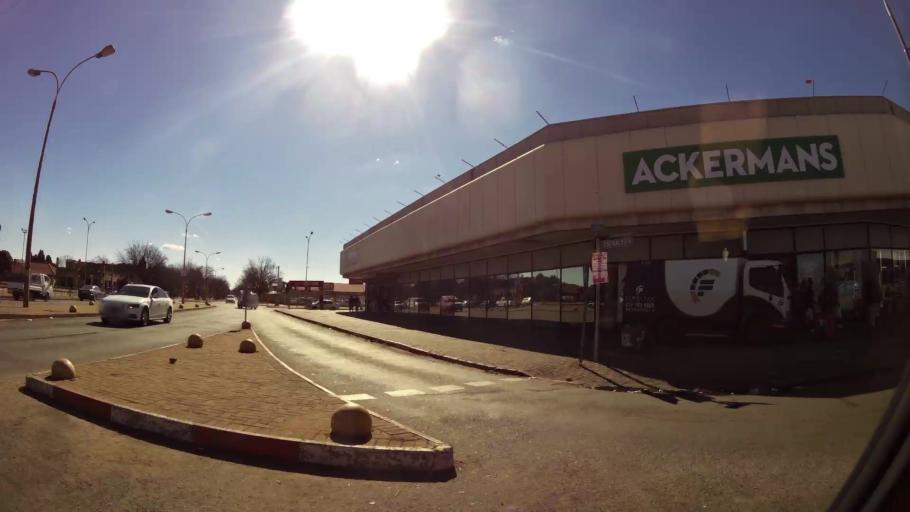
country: ZA
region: Gauteng
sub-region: West Rand District Municipality
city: Carletonville
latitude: -26.3565
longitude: 27.3962
